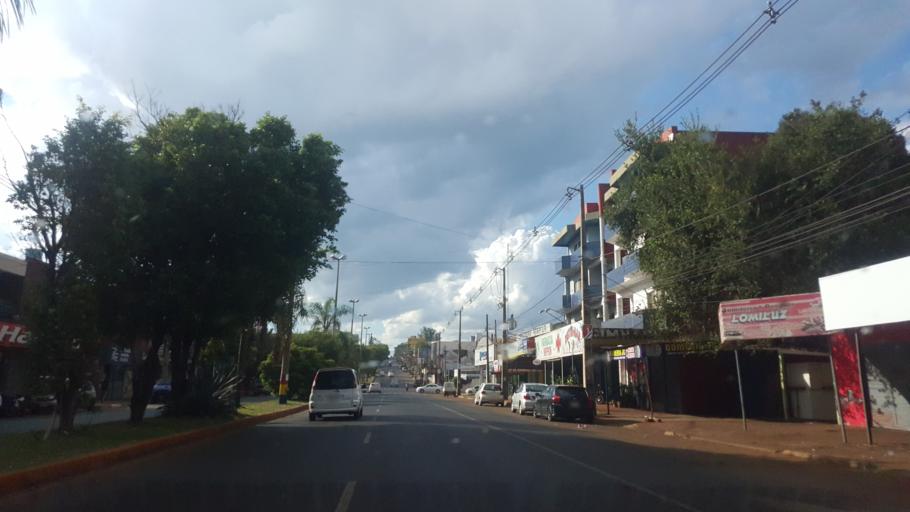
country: PY
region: Itapua
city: Encarnacion
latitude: -27.3359
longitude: -55.8584
